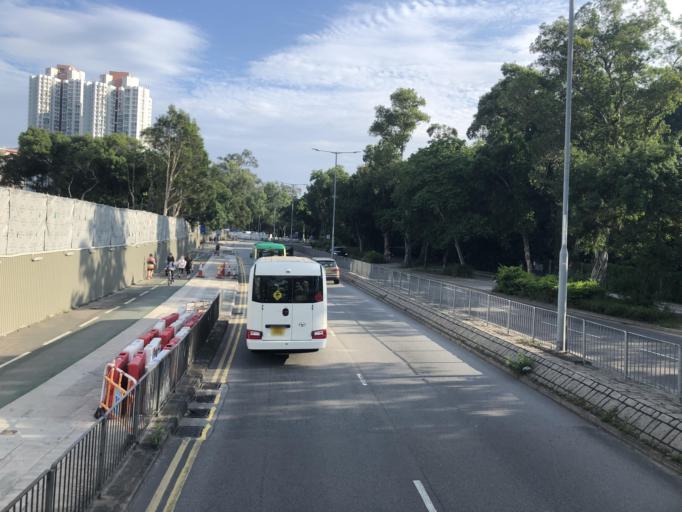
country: HK
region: Tai Po
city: Tai Po
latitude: 22.4990
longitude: 114.1231
